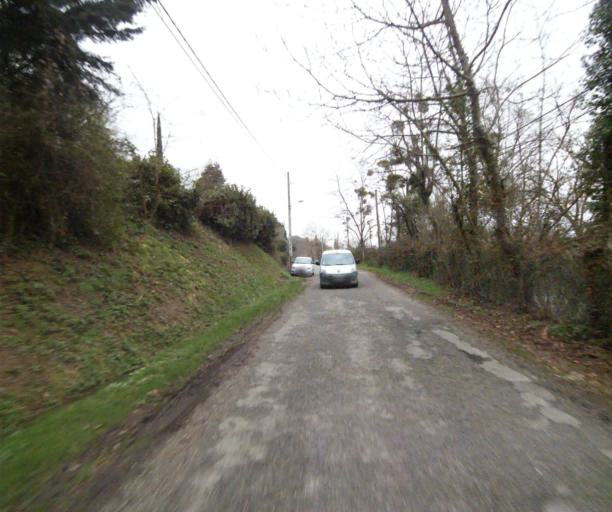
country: FR
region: Midi-Pyrenees
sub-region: Departement de l'Ariege
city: Saverdun
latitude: 43.2269
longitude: 1.5826
